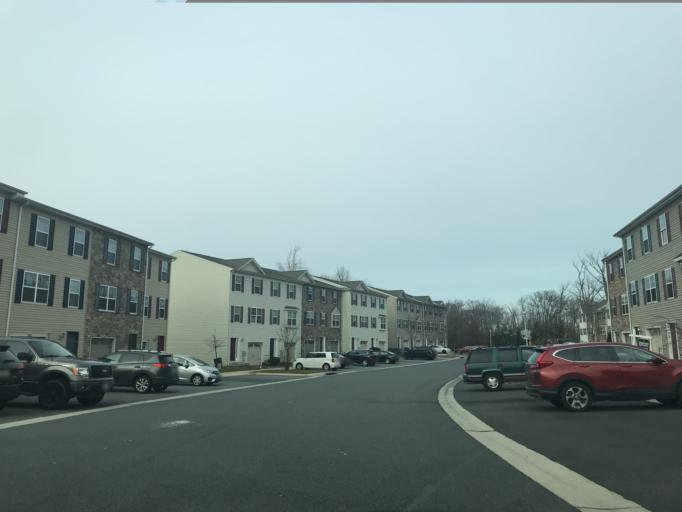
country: US
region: Maryland
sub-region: Cecil County
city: Elkton
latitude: 39.6132
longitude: -75.8053
